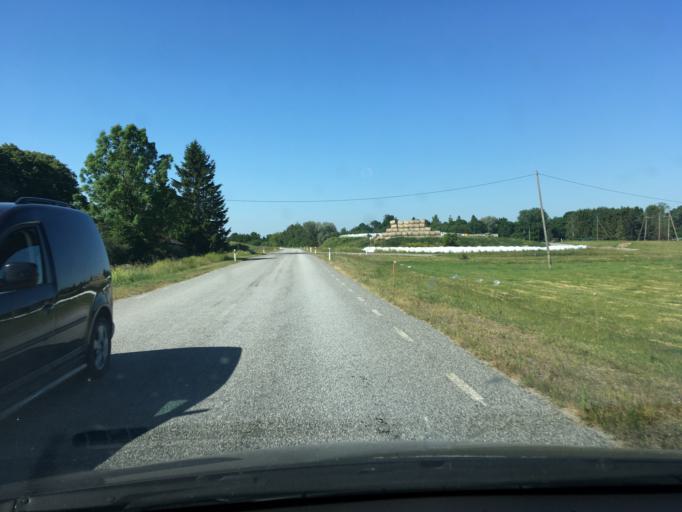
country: EE
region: Harju
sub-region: Raasiku vald
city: Raasiku
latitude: 59.3996
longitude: 25.1946
